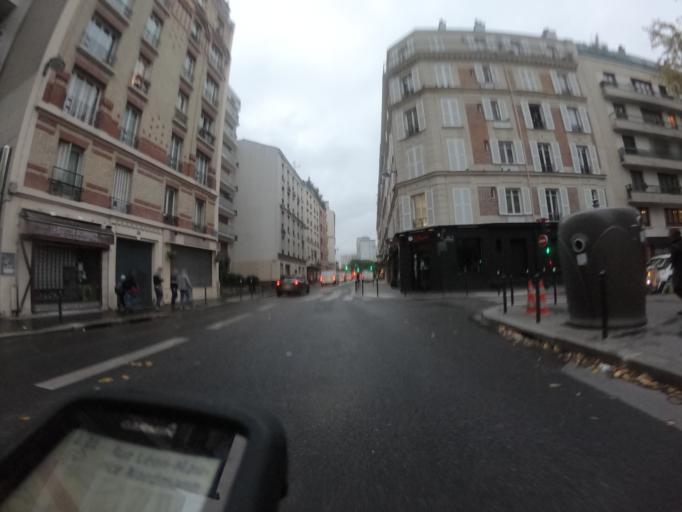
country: FR
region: Ile-de-France
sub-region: Departement du Val-de-Marne
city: Gentilly
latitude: 48.8251
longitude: 2.3417
